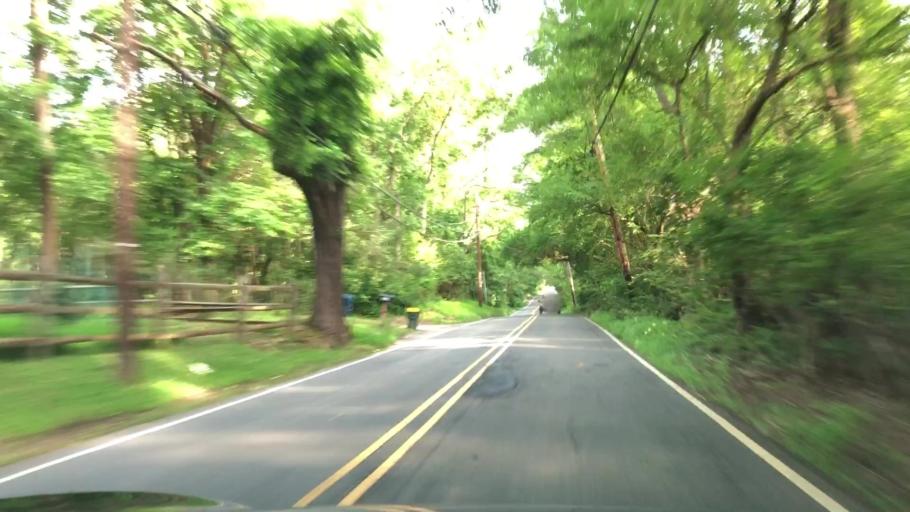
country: US
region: New Jersey
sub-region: Mercer County
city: Princeton
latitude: 40.3390
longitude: -74.7025
